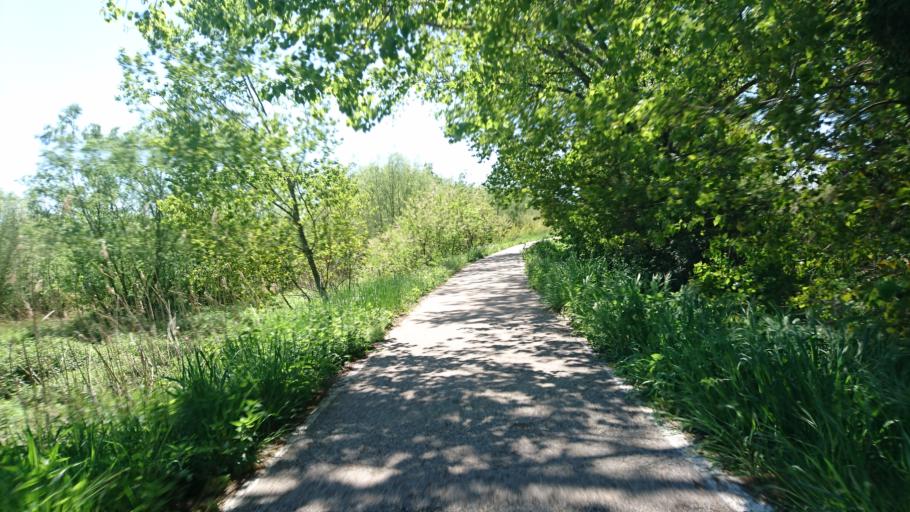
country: IT
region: The Marches
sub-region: Provincia di Pesaro e Urbino
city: Pesaro
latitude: 43.9074
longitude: 12.8754
